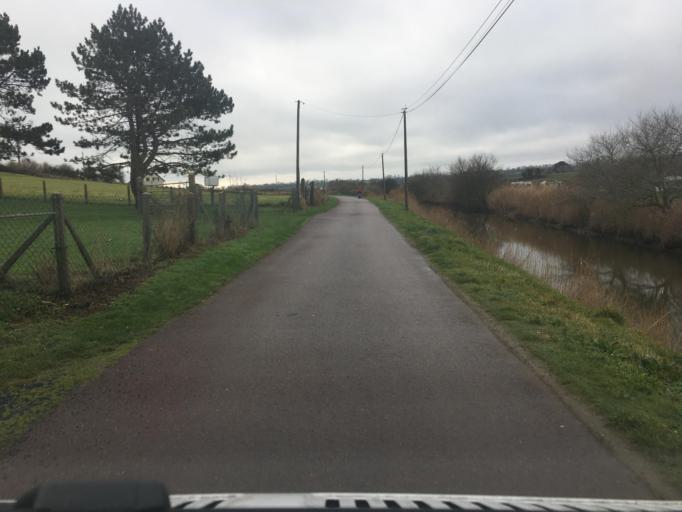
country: FR
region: Lower Normandy
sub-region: Departement du Calvados
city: Grandcamp-Maisy
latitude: 49.3923
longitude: -1.0194
